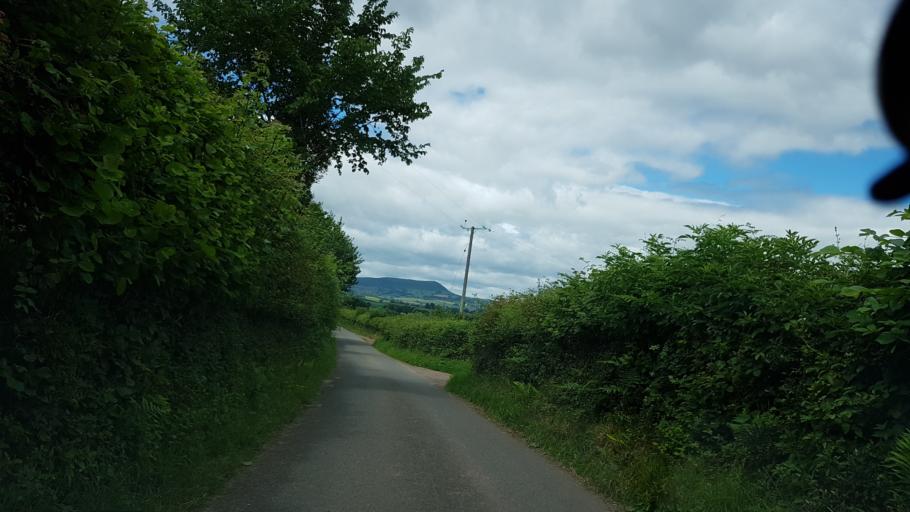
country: GB
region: Wales
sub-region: Monmouthshire
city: Llanarth
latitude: 51.8224
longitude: -2.8643
